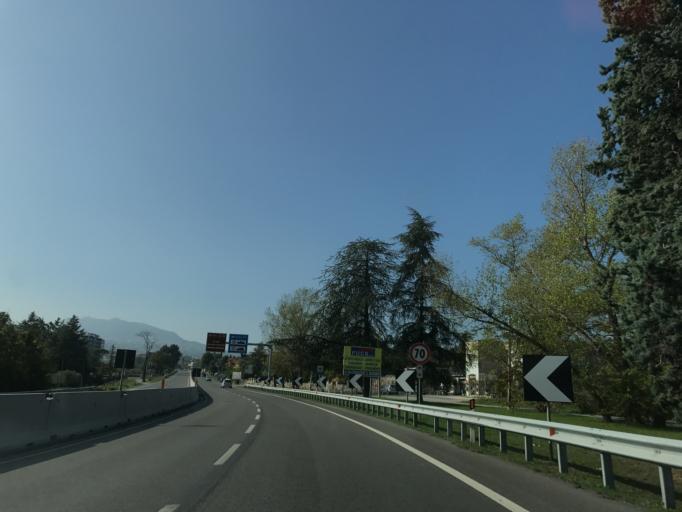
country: SM
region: Serravalle
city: Serravalle
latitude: 43.9881
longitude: 12.4974
